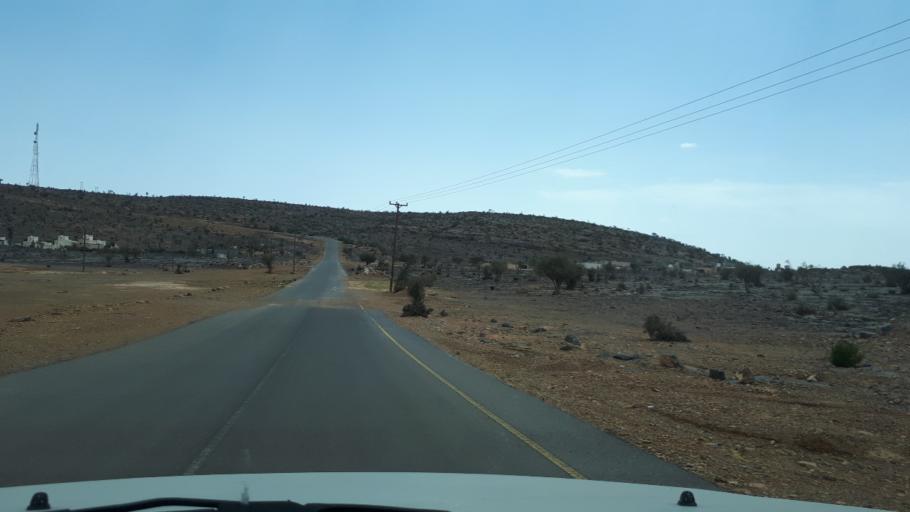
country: OM
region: Muhafazat ad Dakhiliyah
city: Bahla'
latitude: 23.2204
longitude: 57.2013
